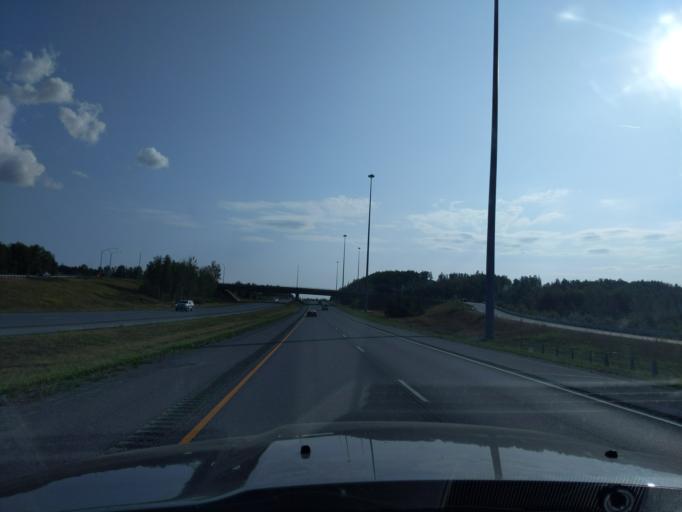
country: US
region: Alaska
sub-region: Anchorage Municipality
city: Eagle River
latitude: 61.3442
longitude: -149.5618
